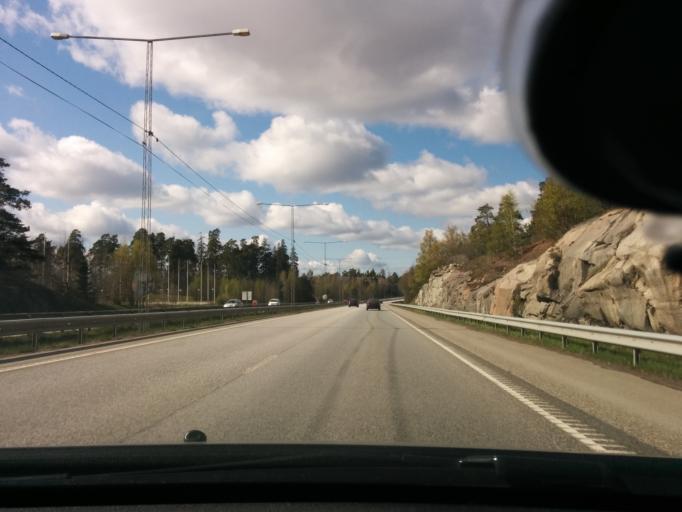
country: SE
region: Stockholm
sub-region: Jarfalla Kommun
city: Jakobsberg
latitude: 59.4543
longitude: 17.8325
